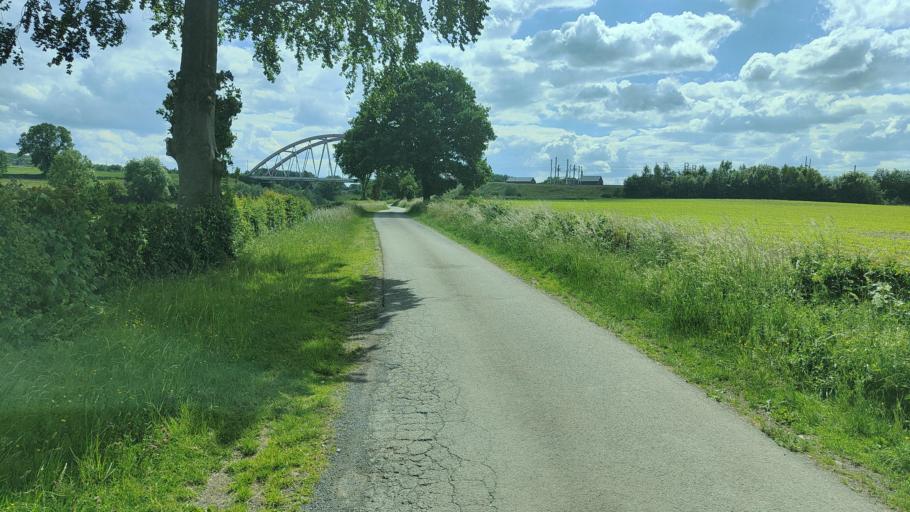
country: BE
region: Wallonia
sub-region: Province de Liege
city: La Calamine
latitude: 50.7007
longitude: 6.0516
